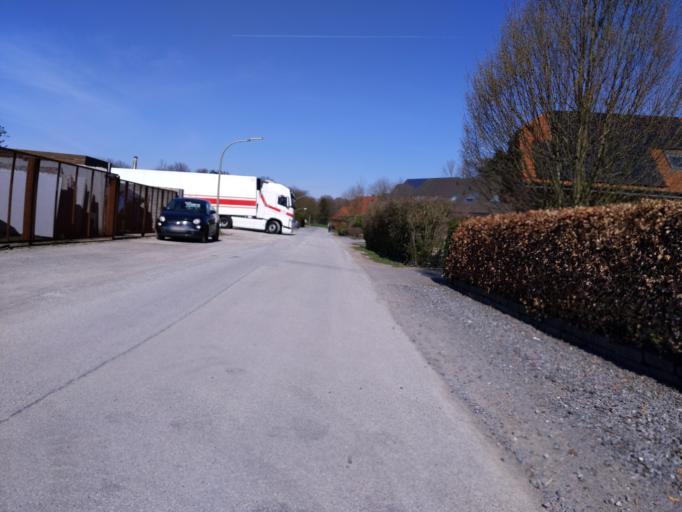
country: DE
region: North Rhine-Westphalia
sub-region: Regierungsbezirk Dusseldorf
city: Schermbeck
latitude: 51.6970
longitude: 6.8887
